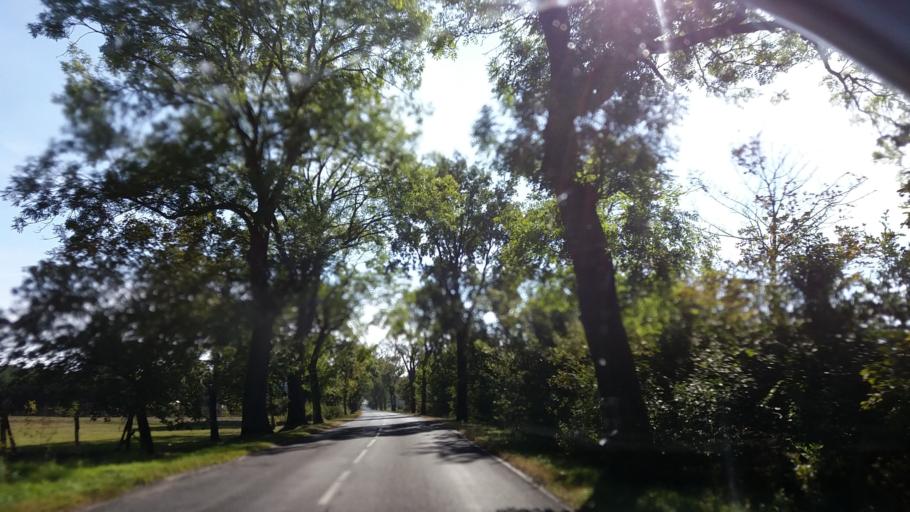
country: PL
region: Lubusz
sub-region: Powiat strzelecko-drezdenecki
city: Drezdenko
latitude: 52.7925
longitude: 15.8358
